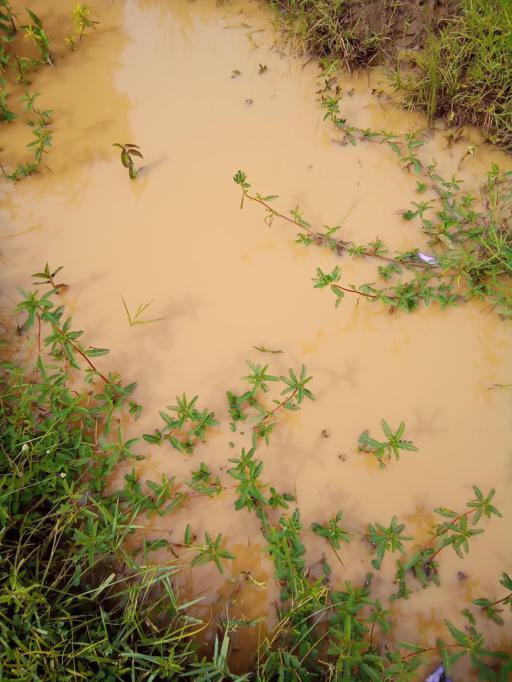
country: KE
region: Homa Bay
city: Homa Bay
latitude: -0.5015
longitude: 34.1656
